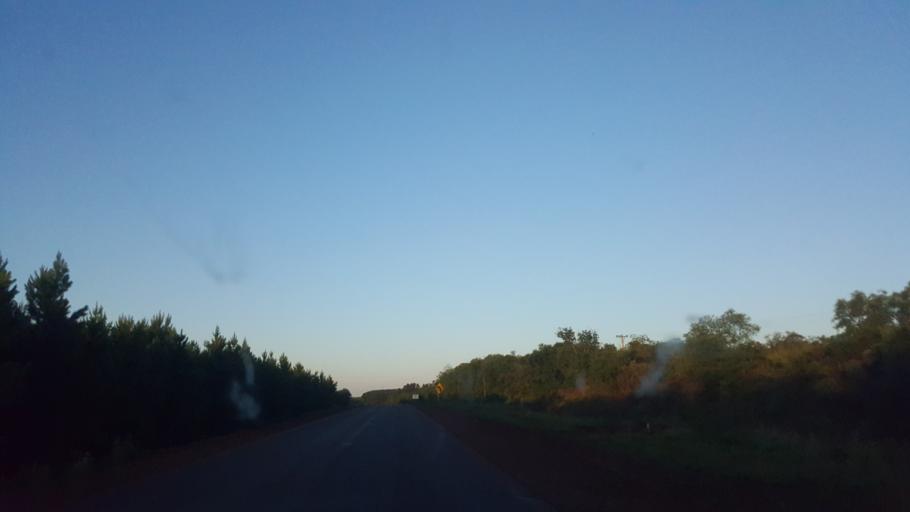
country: AR
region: Corrientes
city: Santo Tome
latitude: -28.4321
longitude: -55.9966
